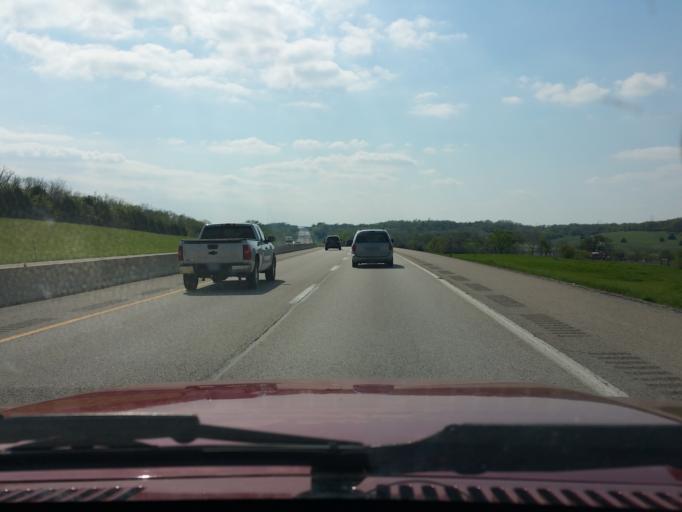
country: US
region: Kansas
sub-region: Douglas County
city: Lawrence
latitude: 38.9976
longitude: -95.2883
